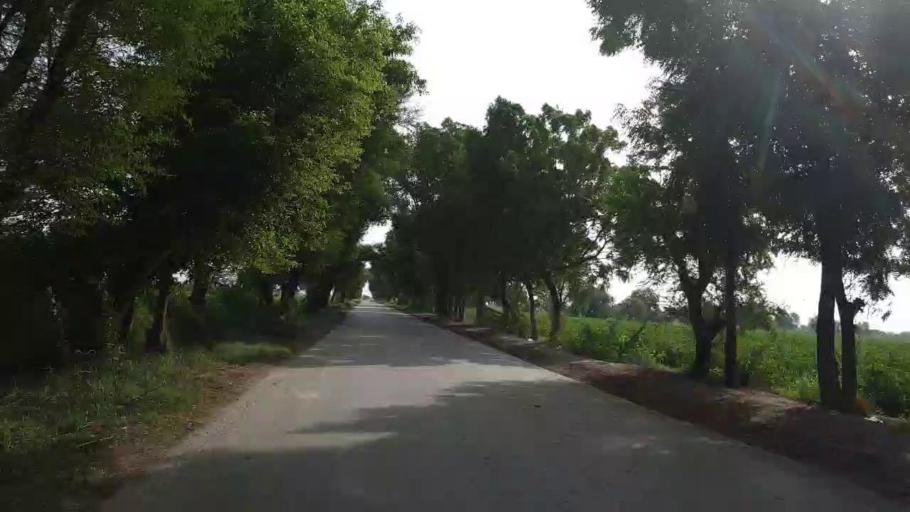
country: PK
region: Sindh
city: Nawabshah
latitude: 26.2526
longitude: 68.4637
